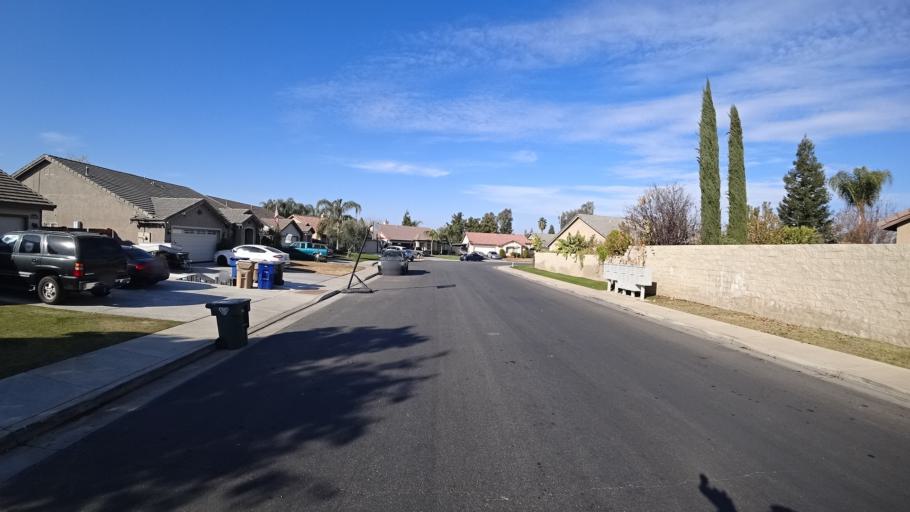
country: US
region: California
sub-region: Kern County
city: Greenacres
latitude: 35.3996
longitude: -119.0961
